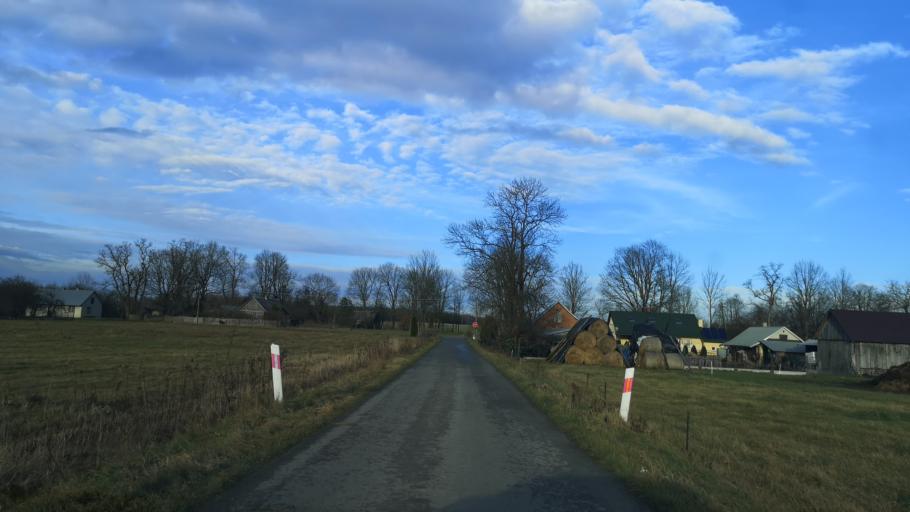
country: PL
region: Subcarpathian Voivodeship
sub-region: Powiat lezajski
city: Piskorowice
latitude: 50.2625
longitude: 22.5879
